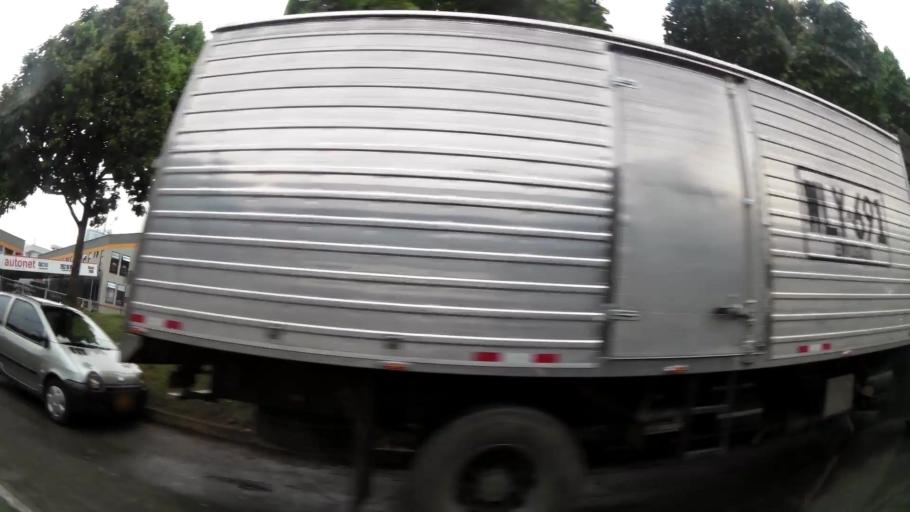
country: CO
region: Antioquia
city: Medellin
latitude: 6.2229
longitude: -75.5715
